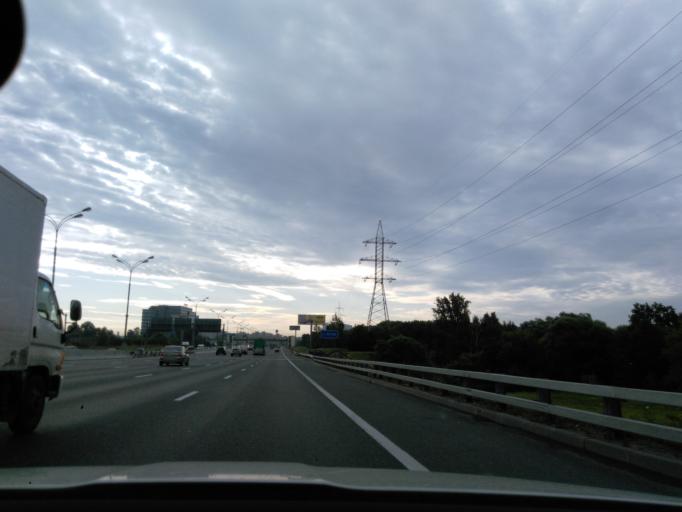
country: RU
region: Moscow
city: Vatutino
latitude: 55.8948
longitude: 37.6835
